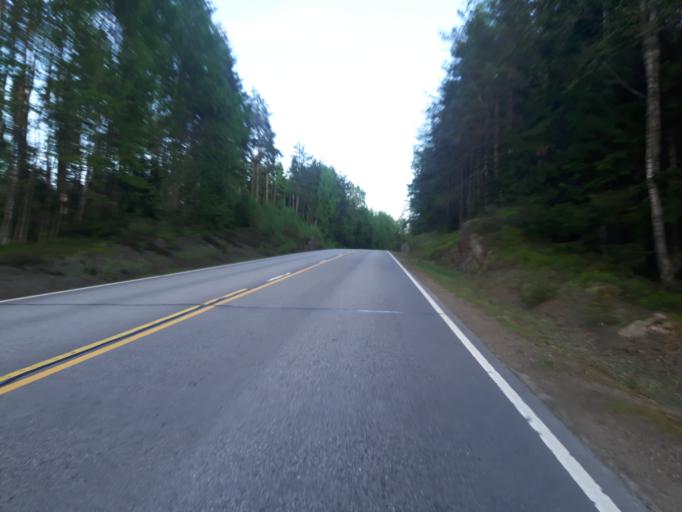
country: FI
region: Uusimaa
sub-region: Loviisa
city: Perna
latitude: 60.4596
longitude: 26.0653
